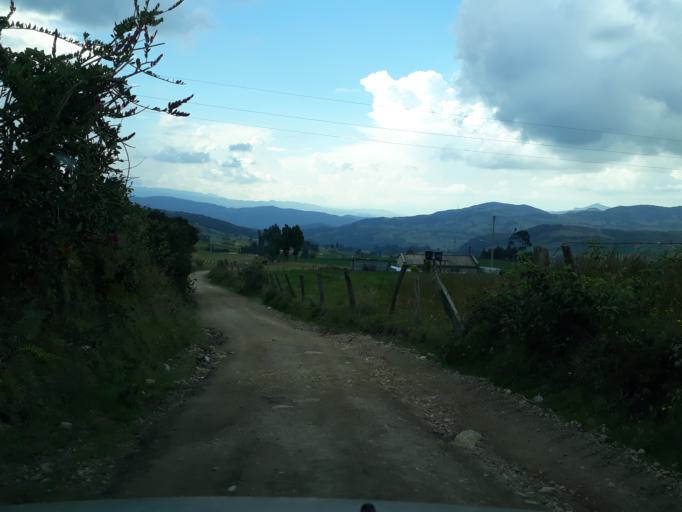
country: CO
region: Cundinamarca
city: Villapinzon
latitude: 5.2353
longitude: -73.6718
